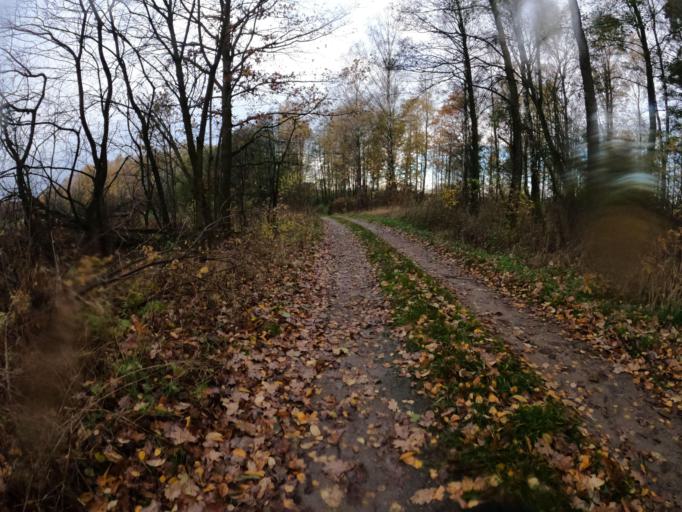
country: PL
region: West Pomeranian Voivodeship
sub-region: Powiat walecki
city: Tuczno
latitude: 53.2050
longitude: 16.2047
